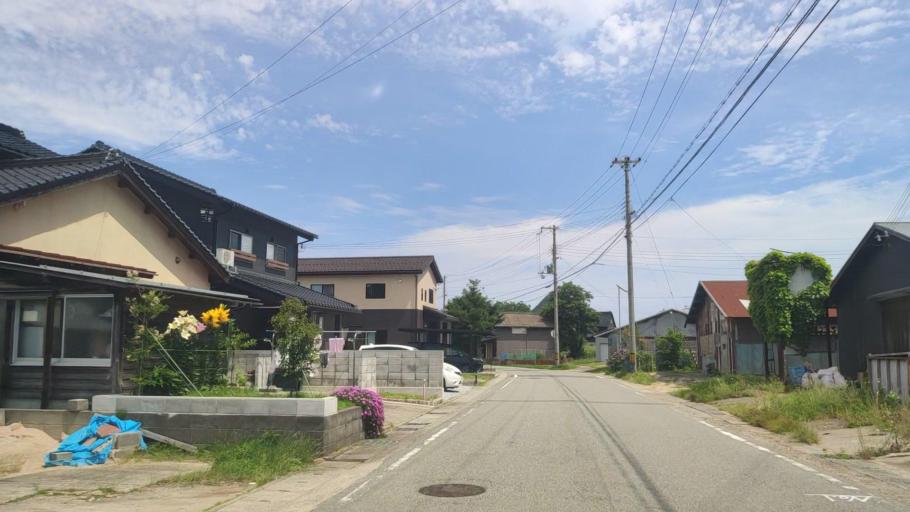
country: JP
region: Hyogo
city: Toyooka
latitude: 35.6543
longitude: 134.7629
